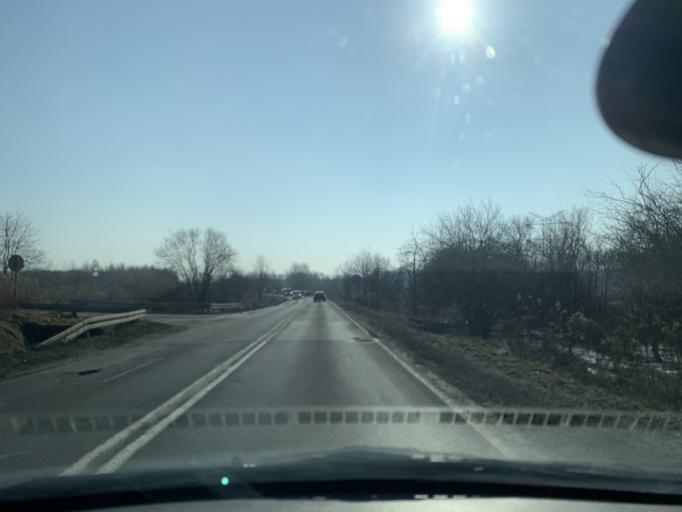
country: PL
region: Silesian Voivodeship
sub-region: Piekary Slaskie
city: Piekary Slaskie
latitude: 50.3823
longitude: 18.9262
